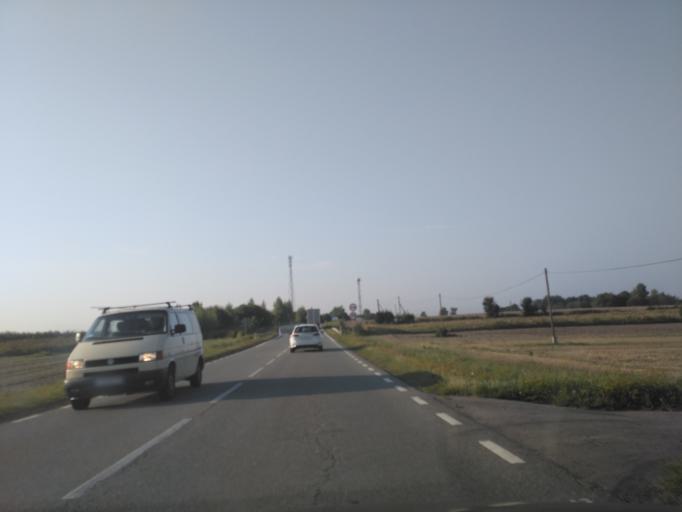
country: PL
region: Lublin Voivodeship
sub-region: Powiat janowski
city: Modliborzyce
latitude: 50.7721
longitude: 22.3251
